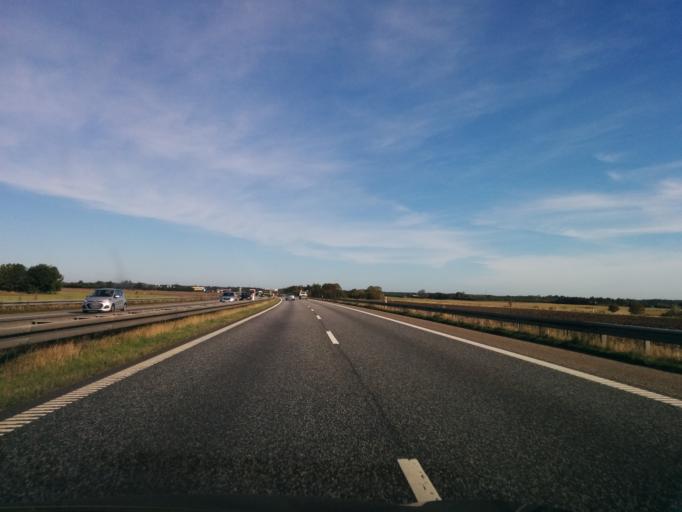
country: DK
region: Central Jutland
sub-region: Hedensted Kommune
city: Hedensted
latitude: 55.7722
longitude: 9.6470
